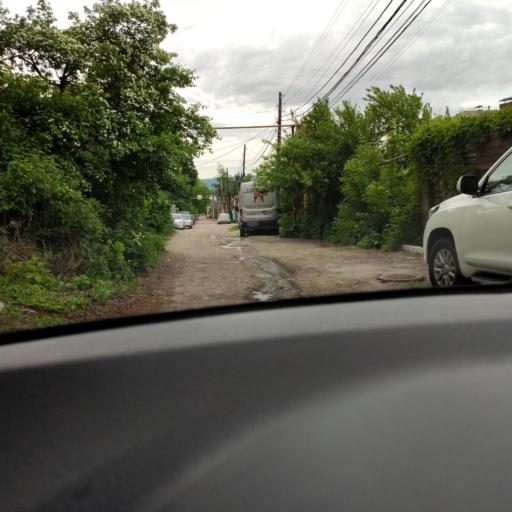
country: RU
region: Samara
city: Samara
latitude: 53.2746
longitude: 50.1994
